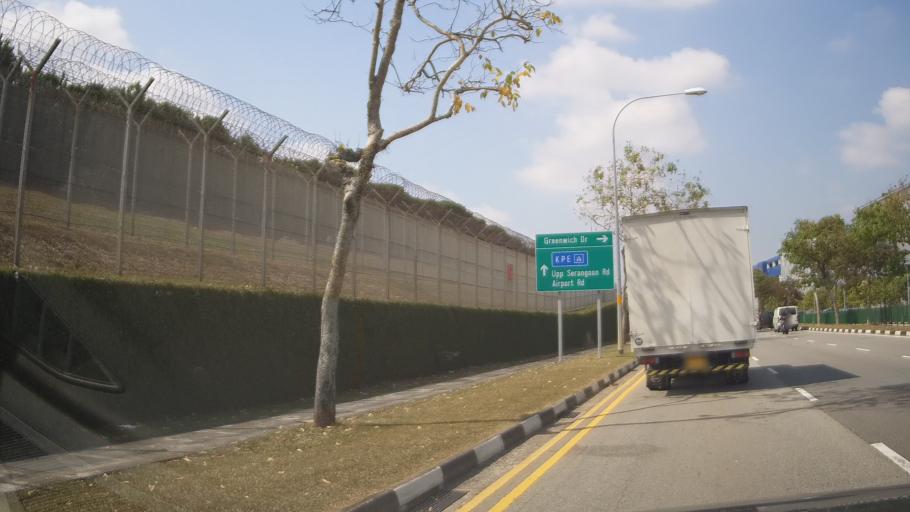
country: SG
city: Singapore
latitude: 1.3723
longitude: 103.9119
